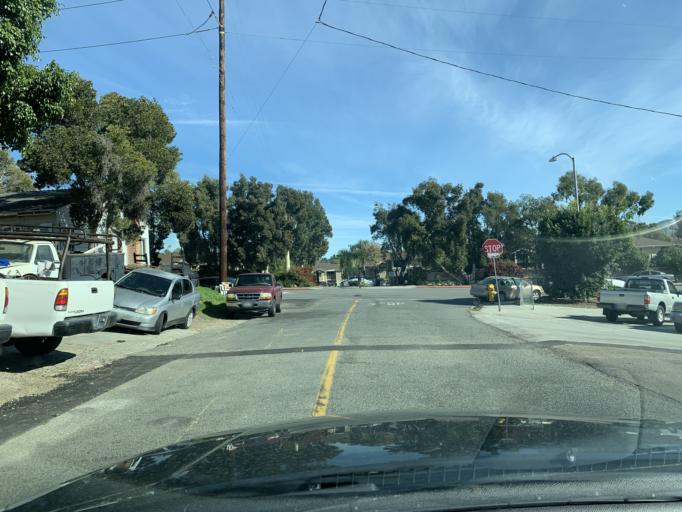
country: US
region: California
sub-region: San Diego County
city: Lemon Grove
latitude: 32.7446
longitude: -117.0277
